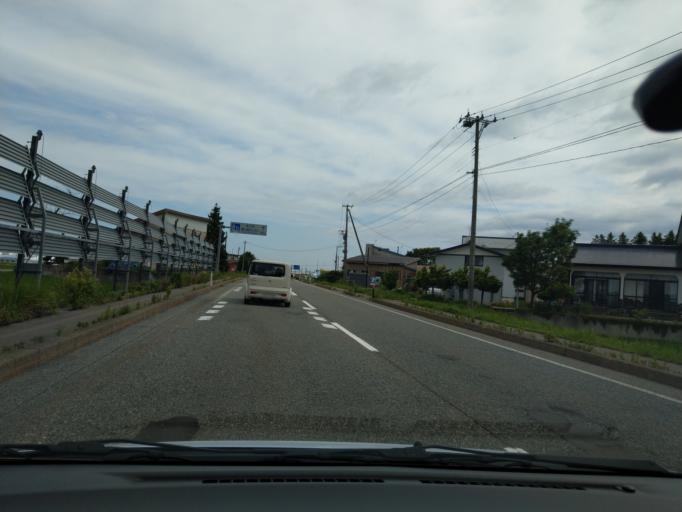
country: JP
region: Akita
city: Yokotemachi
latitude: 39.3749
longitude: 140.5688
